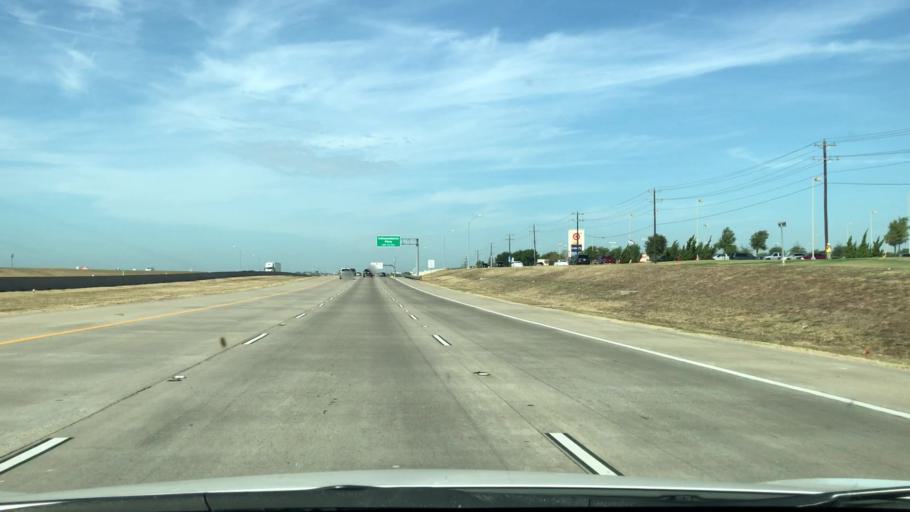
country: US
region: Texas
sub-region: Collin County
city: Allen
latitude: 33.1284
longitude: -96.7241
